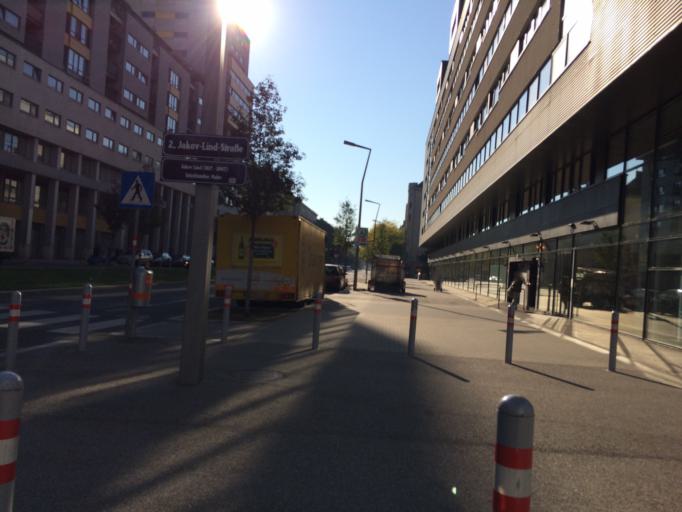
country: AT
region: Vienna
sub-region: Wien Stadt
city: Vienna
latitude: 48.2261
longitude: 16.3993
